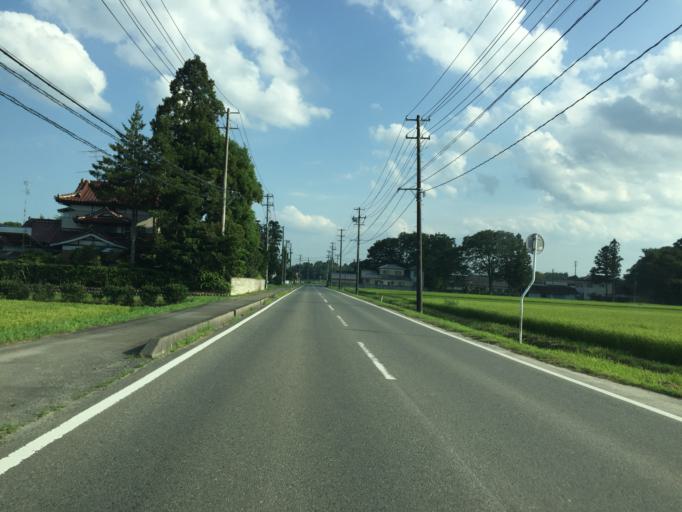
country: JP
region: Miyagi
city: Marumori
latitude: 37.7842
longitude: 140.9143
